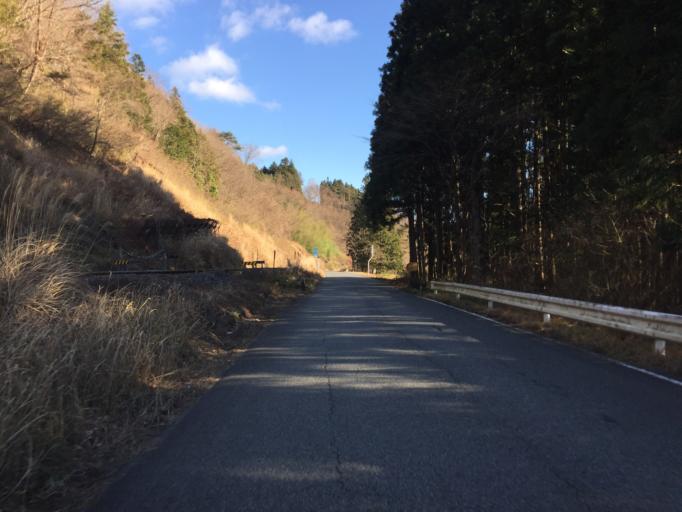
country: JP
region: Fukushima
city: Iwaki
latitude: 37.2162
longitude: 140.7261
